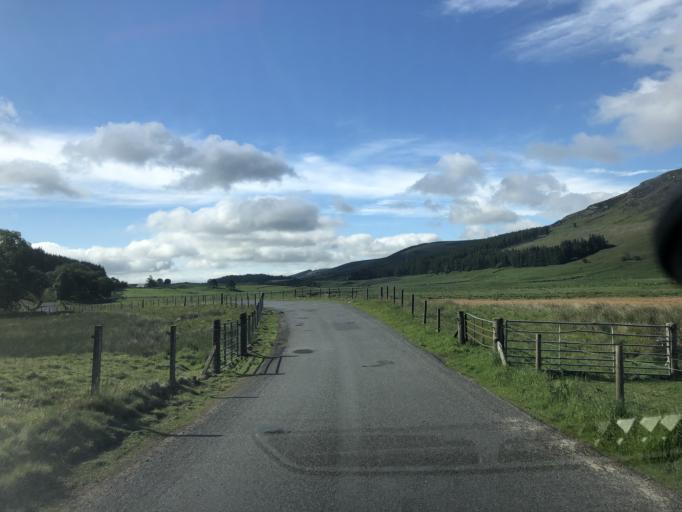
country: GB
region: Scotland
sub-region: Angus
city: Kirriemuir
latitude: 56.7895
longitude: -3.0313
